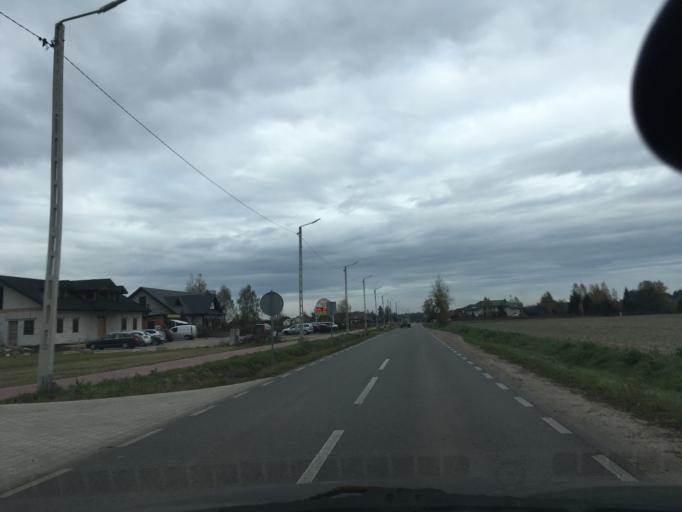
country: PL
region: Lodz Voivodeship
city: Zabia Wola
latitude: 52.0183
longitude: 20.7310
